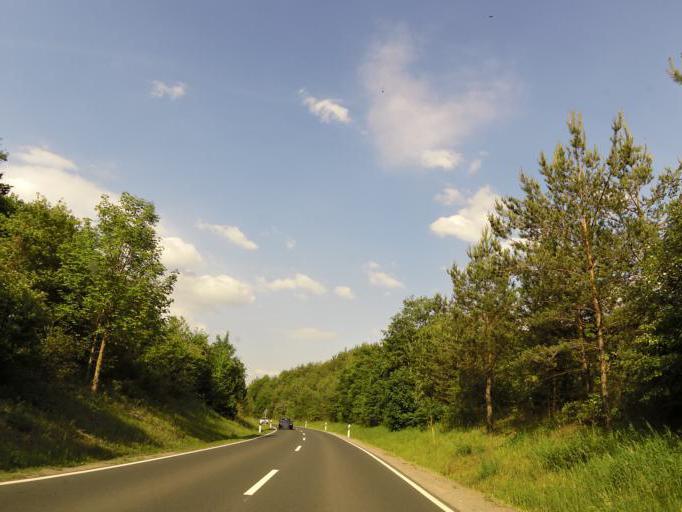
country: DE
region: Bavaria
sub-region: Regierungsbezirk Unterfranken
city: Marktheidenfeld
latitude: 49.8114
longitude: 9.6245
